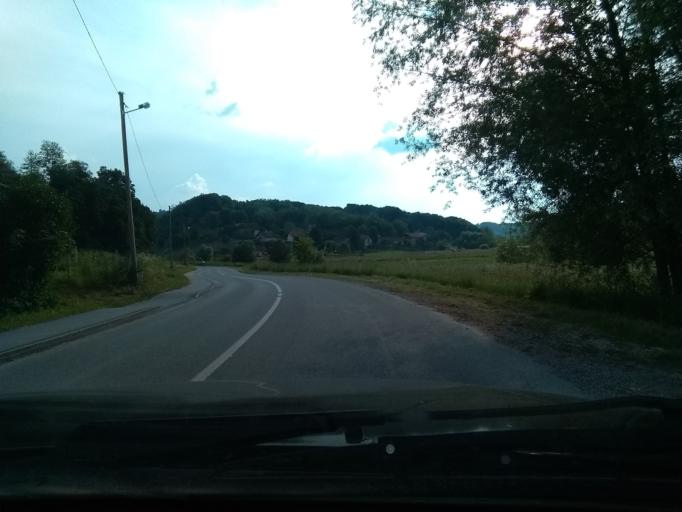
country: SI
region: Bistrica ob Sotli
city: Bistrica ob Sotli
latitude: 46.0749
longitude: 15.7463
